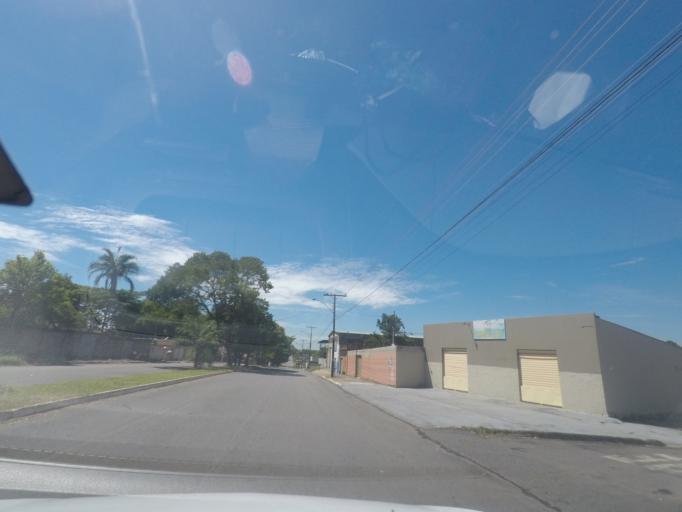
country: BR
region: Goias
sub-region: Aparecida De Goiania
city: Aparecida de Goiania
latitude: -16.7756
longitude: -49.3402
